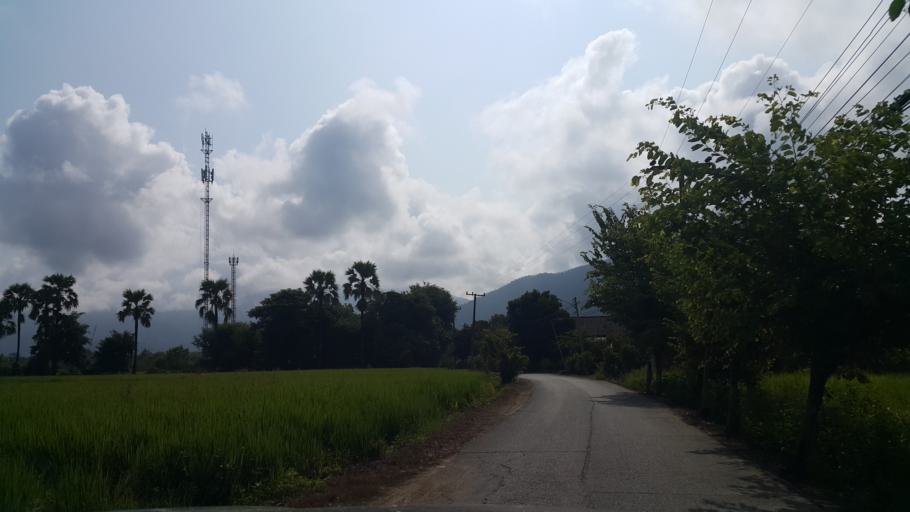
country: TH
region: Chiang Mai
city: Mae On
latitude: 18.7427
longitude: 99.2274
